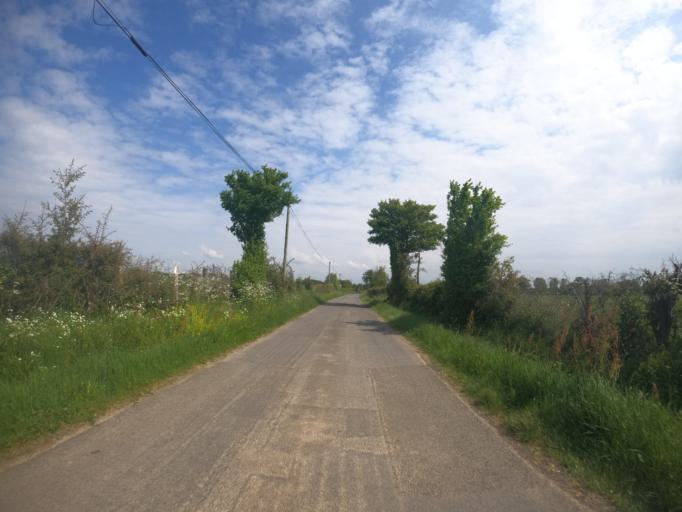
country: FR
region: Poitou-Charentes
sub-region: Departement des Deux-Sevres
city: Saint-Varent
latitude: 46.8934
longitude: -0.2838
